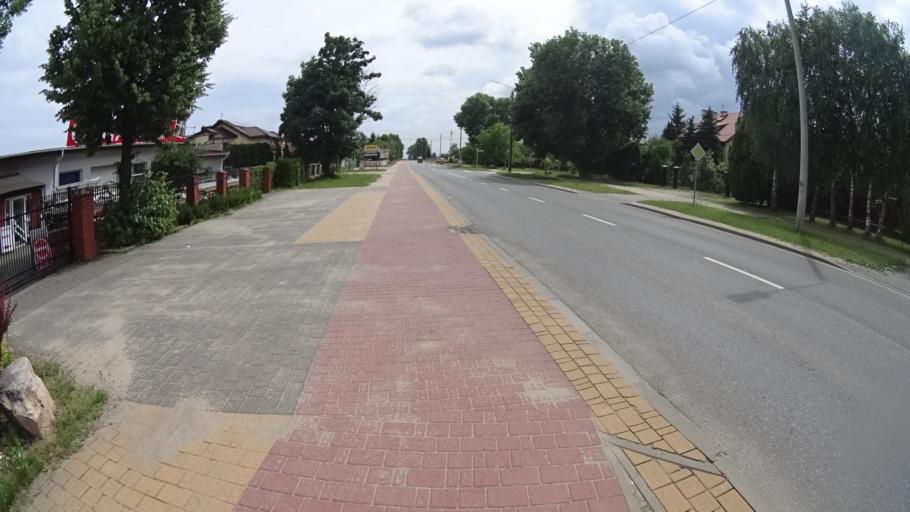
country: PL
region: Masovian Voivodeship
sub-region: Powiat grojecki
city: Grojec
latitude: 51.8539
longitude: 20.8707
